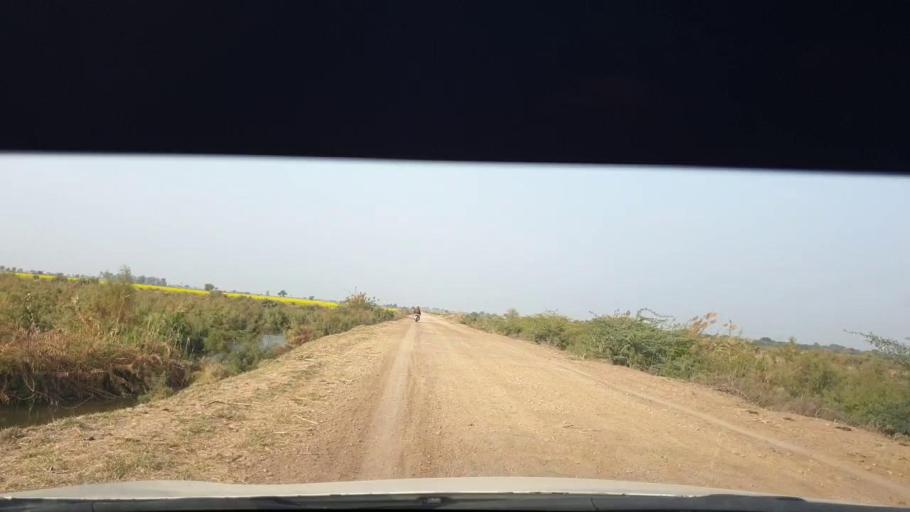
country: PK
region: Sindh
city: Berani
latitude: 25.7518
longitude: 68.9408
